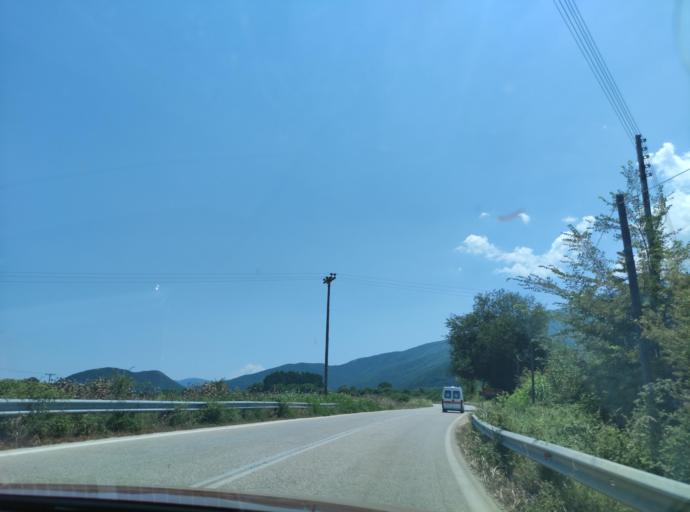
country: GR
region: East Macedonia and Thrace
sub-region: Nomos Kavalas
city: Palaiochori
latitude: 40.9664
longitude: 24.1802
